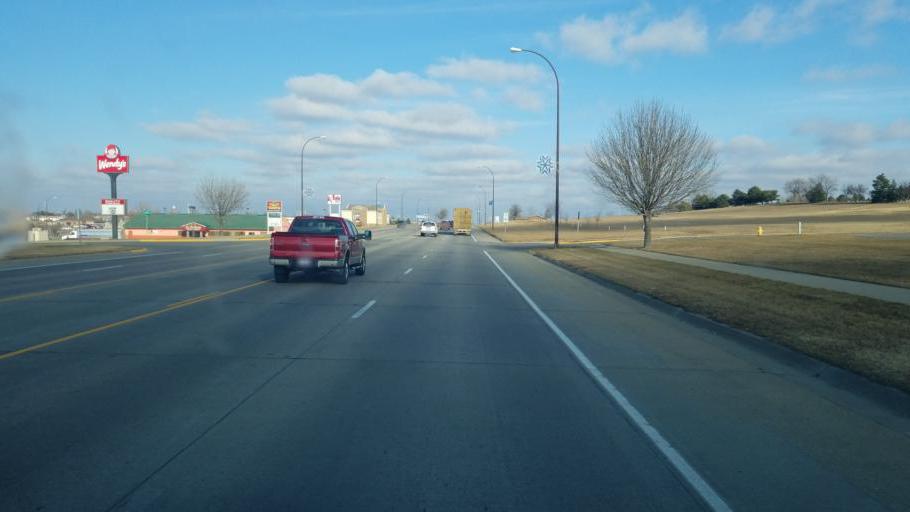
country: US
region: South Dakota
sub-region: Yankton County
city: Yankton
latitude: 42.8973
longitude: -97.3974
